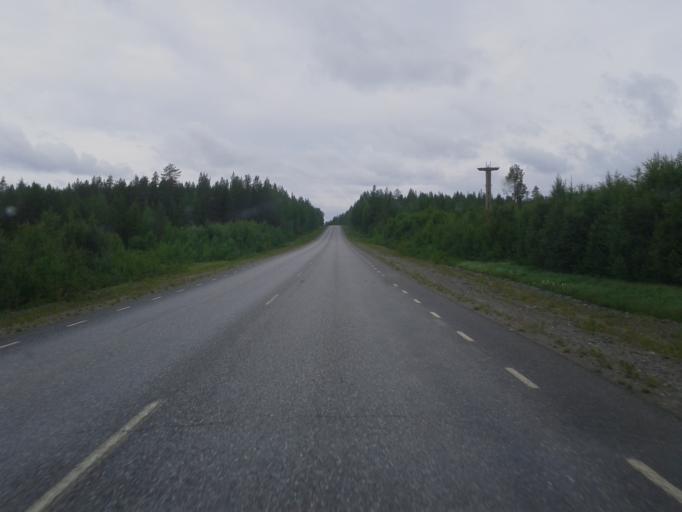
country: SE
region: Vaesterbotten
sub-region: Skelleftea Kommun
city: Langsele
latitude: 64.8854
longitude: 20.2877
